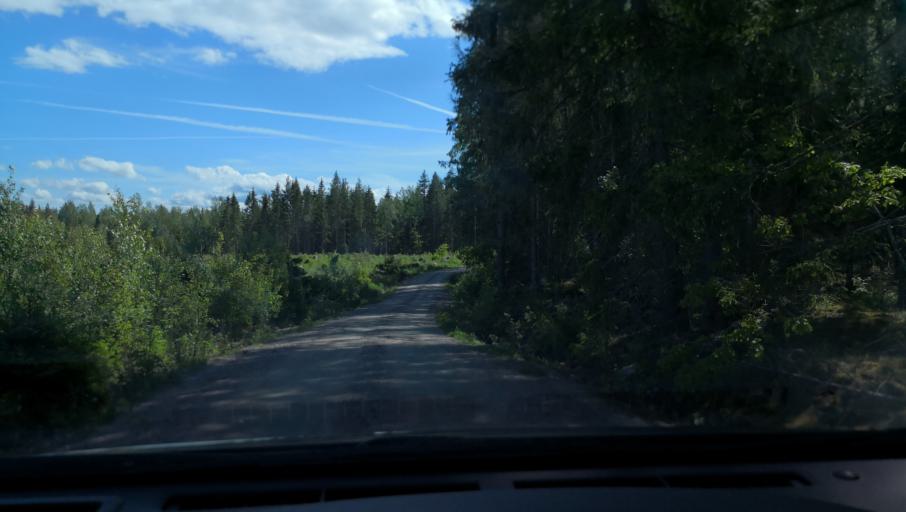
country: SE
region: Vaestmanland
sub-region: Arboga Kommun
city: Tyringe
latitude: 59.3154
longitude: 15.9951
